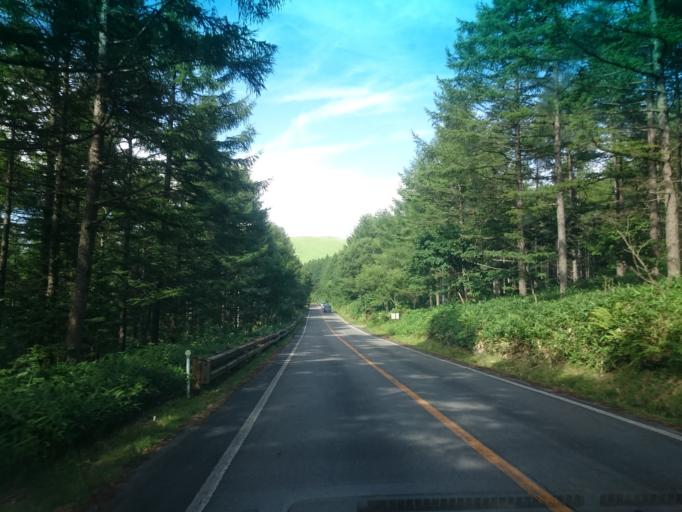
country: JP
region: Nagano
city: Suwa
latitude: 36.1042
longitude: 138.1745
